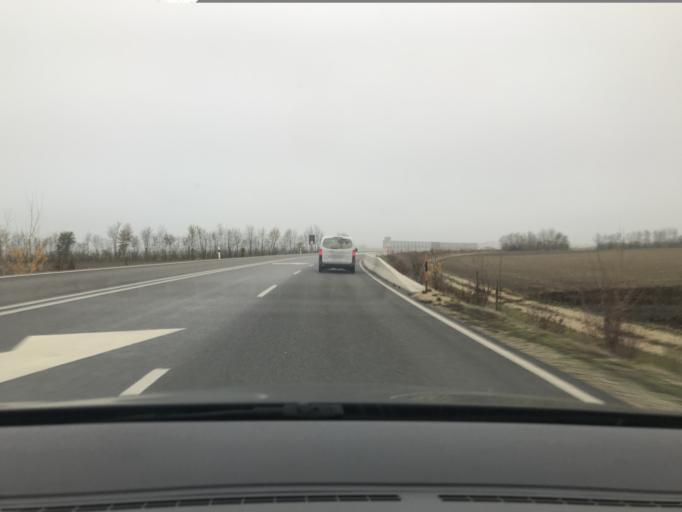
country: DE
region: Bavaria
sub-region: Swabia
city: Wallerstein
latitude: 48.8723
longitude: 10.4570
